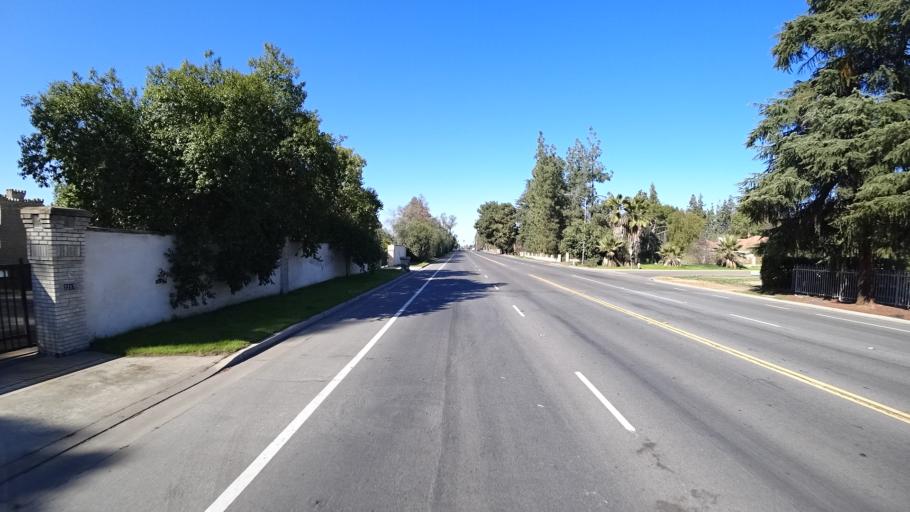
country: US
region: California
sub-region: Fresno County
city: Fresno
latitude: 36.8227
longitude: -119.8326
